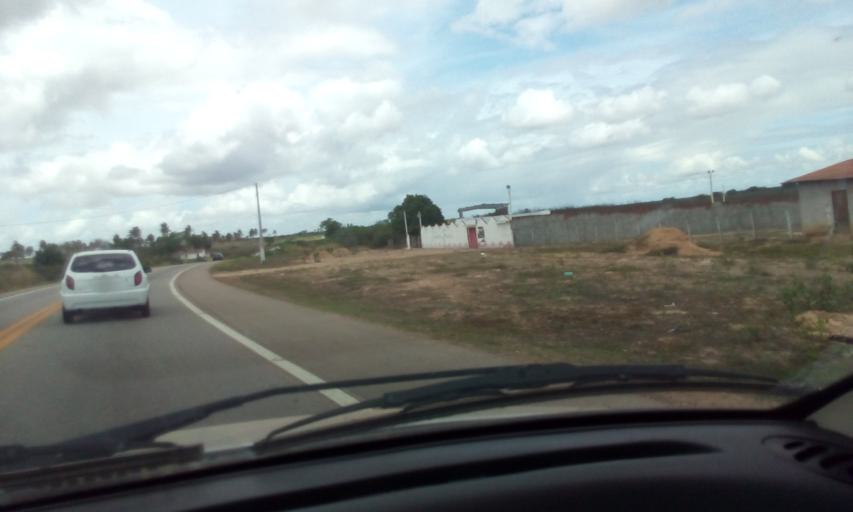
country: BR
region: Rio Grande do Norte
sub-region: Macaiba
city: Macaiba
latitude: -5.9234
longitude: -35.5369
